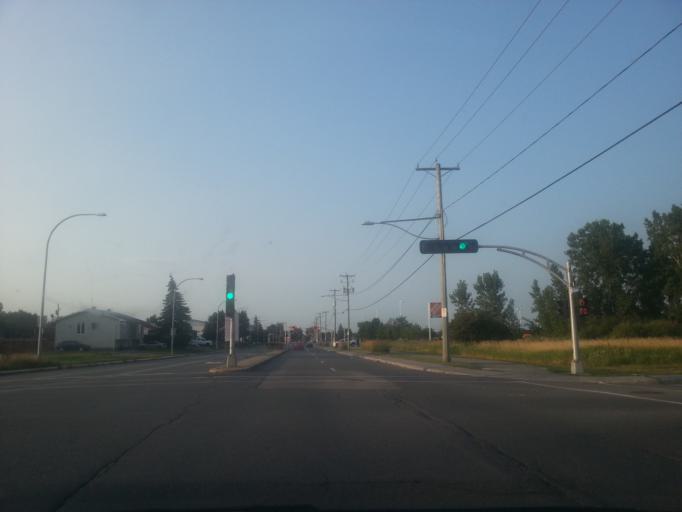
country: CA
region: Quebec
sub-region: Outaouais
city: Gatineau
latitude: 45.4865
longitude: -75.6748
